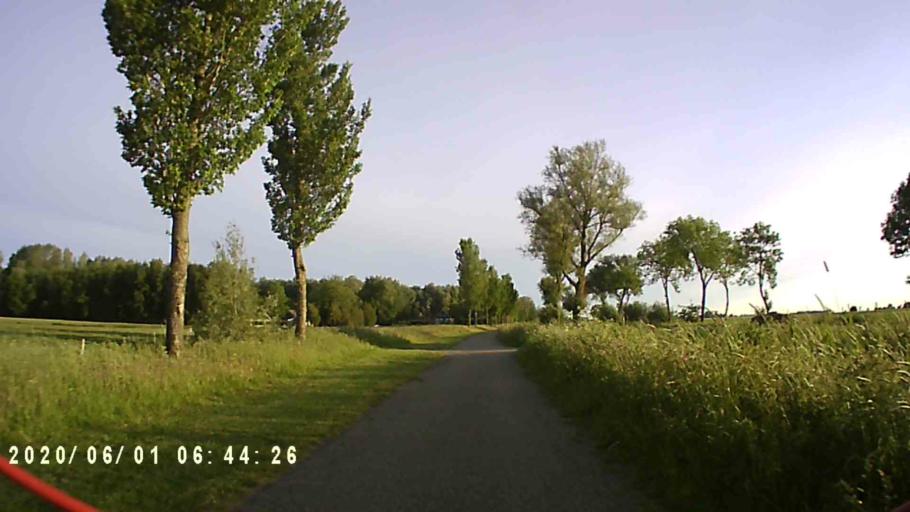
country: NL
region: Friesland
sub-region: Gemeente Kollumerland en Nieuwkruisland
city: Kollum
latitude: 53.3011
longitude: 6.1487
